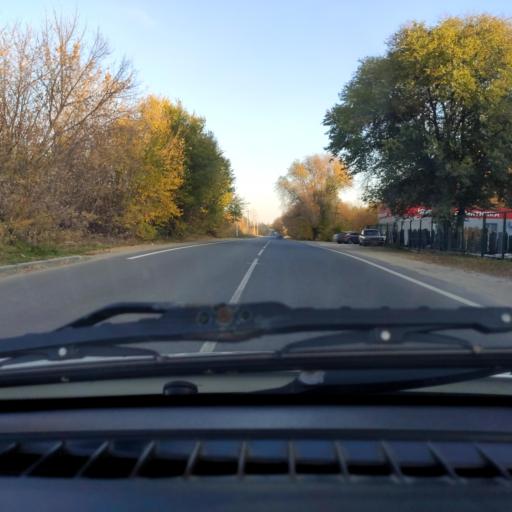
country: RU
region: Samara
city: Tol'yatti
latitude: 53.5082
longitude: 49.4526
